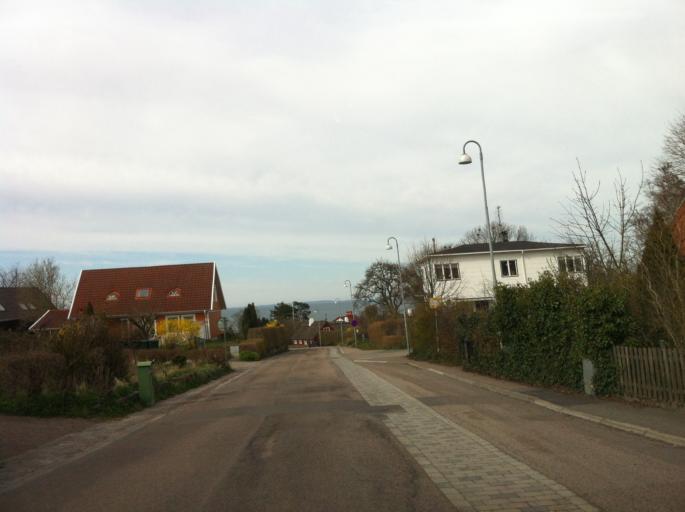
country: SE
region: Skane
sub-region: Hoganas Kommun
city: Hoganas
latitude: 56.2703
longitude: 12.5784
